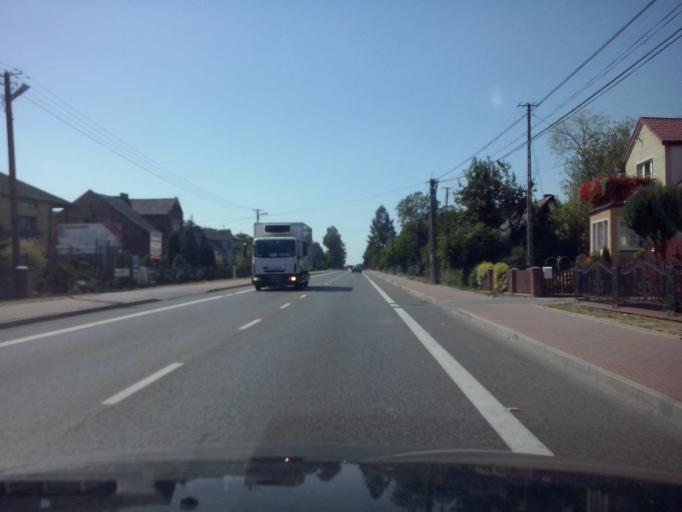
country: PL
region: Swietokrzyskie
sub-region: Powiat kielecki
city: Bieliny
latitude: 50.8492
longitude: 20.9195
